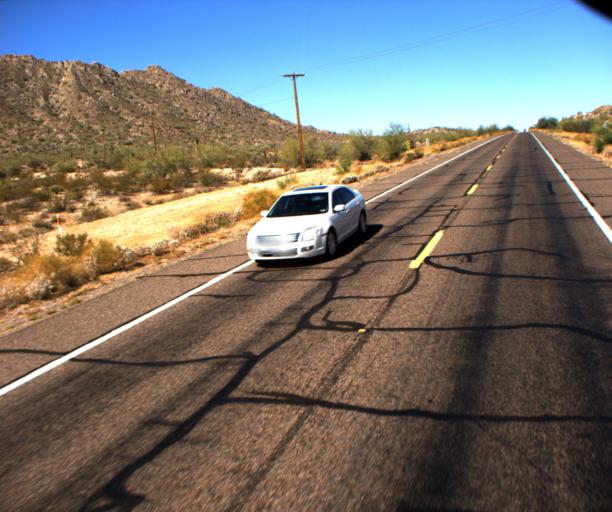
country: US
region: Arizona
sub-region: Pinal County
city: Sacaton
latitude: 33.0146
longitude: -111.6774
